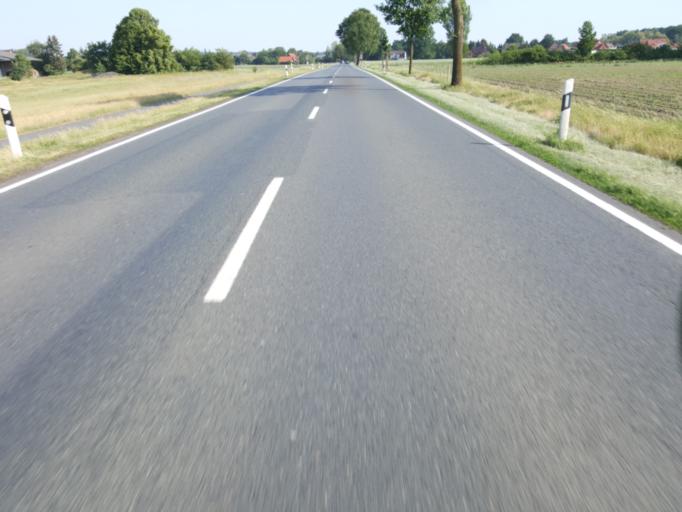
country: DE
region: Lower Saxony
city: Estorf
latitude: 52.5792
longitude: 9.1396
